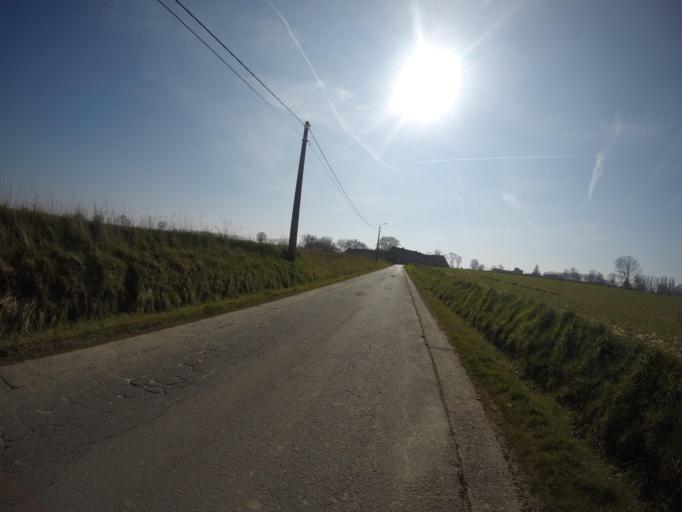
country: BE
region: Flanders
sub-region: Provincie Oost-Vlaanderen
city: Geraardsbergen
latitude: 50.7788
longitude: 3.8393
